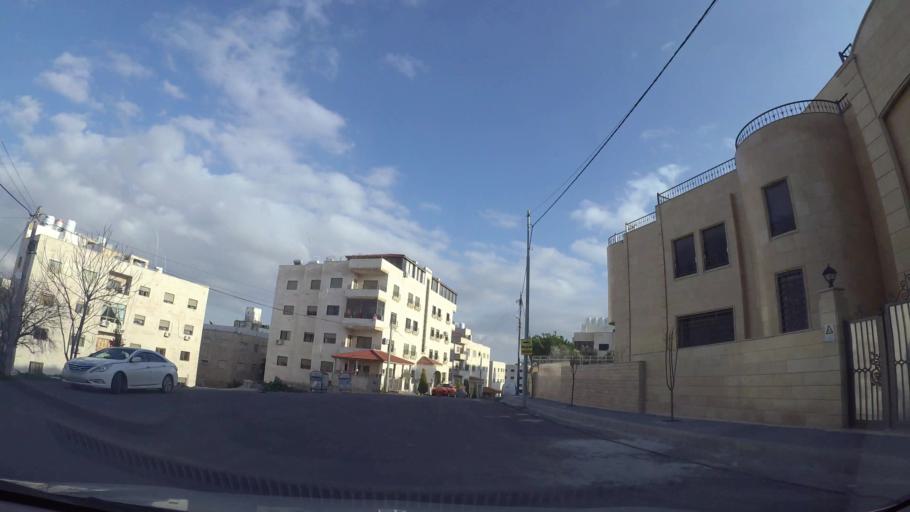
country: JO
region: Amman
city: Al Jubayhah
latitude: 32.0047
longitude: 35.8682
